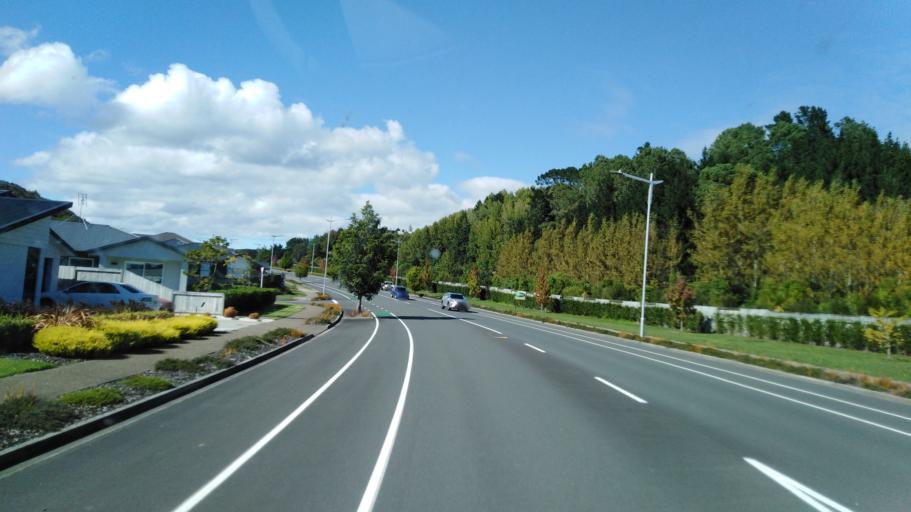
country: NZ
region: Bay of Plenty
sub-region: Tauranga City
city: Tauranga
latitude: -37.7594
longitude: 176.1038
